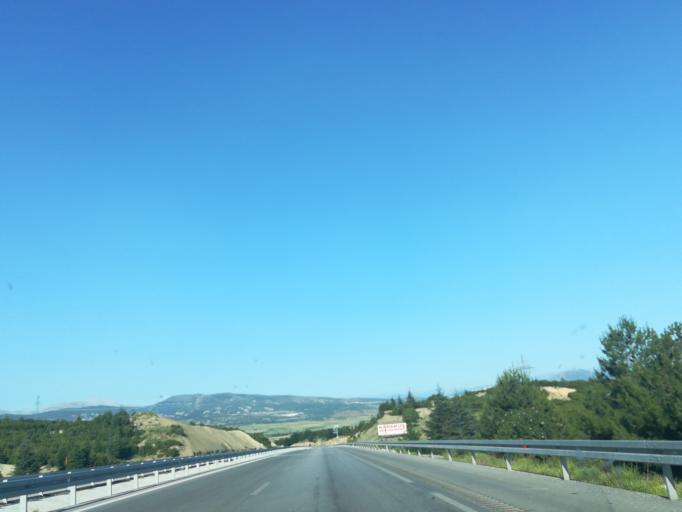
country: TR
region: Isparta
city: Keciborlu
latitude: 37.9161
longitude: 30.2869
